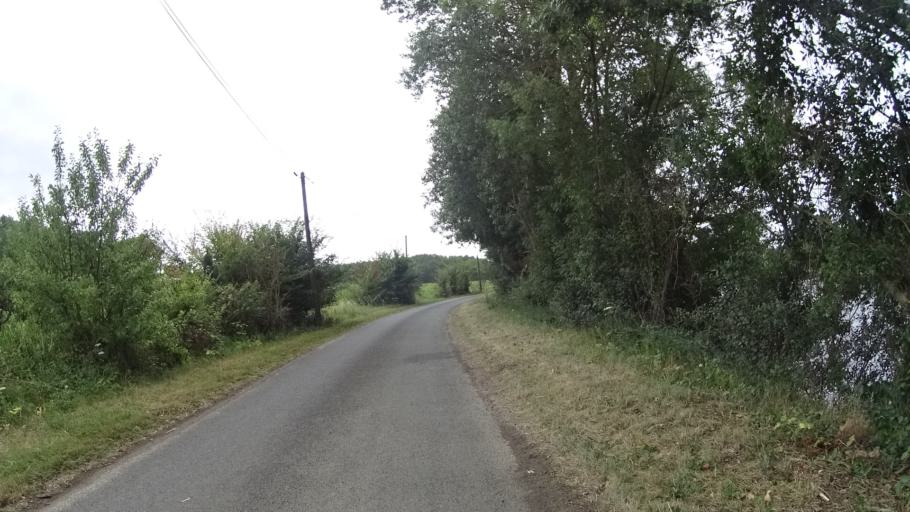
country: FR
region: Pays de la Loire
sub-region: Departement de Maine-et-Loire
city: Montjean-sur-Loire
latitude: 47.3836
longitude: -0.8349
